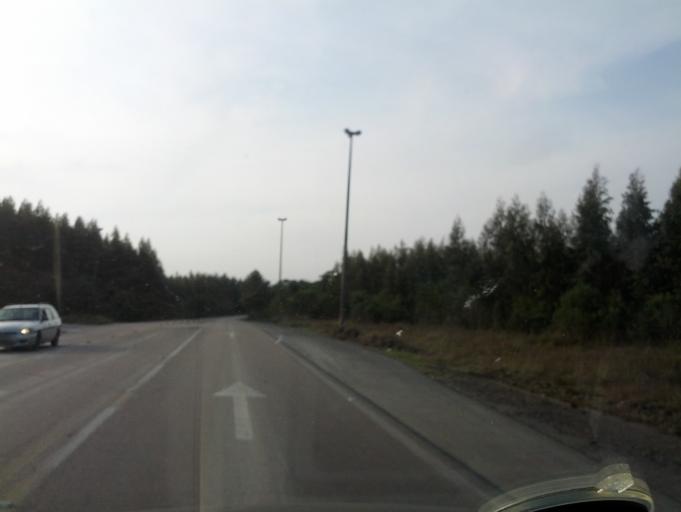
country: BR
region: Santa Catarina
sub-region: Otacilio Costa
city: Otacilio Costa
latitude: -27.4462
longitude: -50.1251
